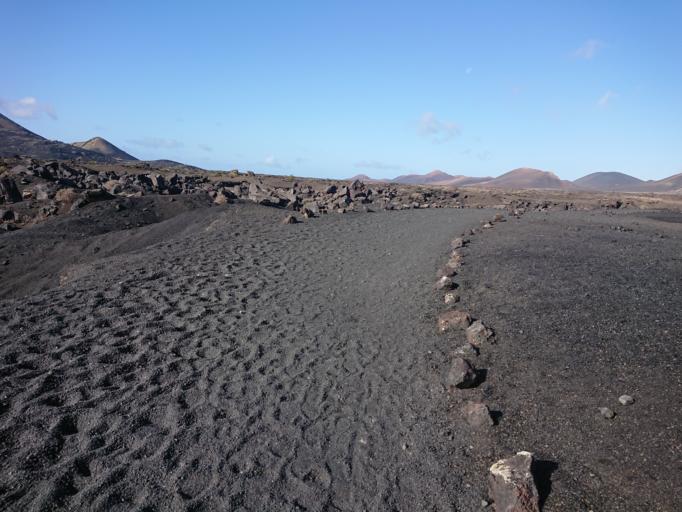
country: ES
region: Canary Islands
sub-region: Provincia de Las Palmas
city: Tias
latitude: 28.9887
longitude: -13.6948
